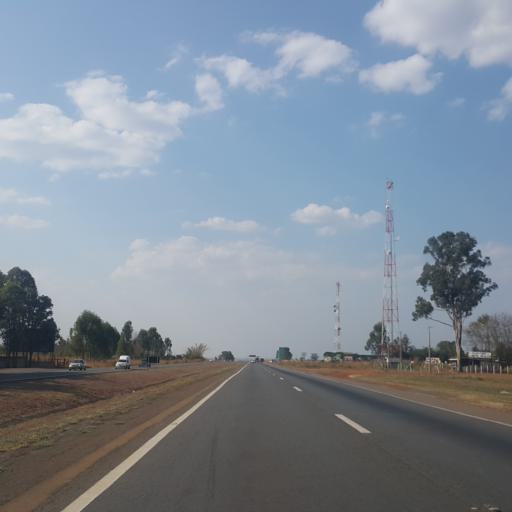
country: BR
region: Goias
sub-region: Abadiania
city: Abadiania
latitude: -16.2207
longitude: -48.7496
